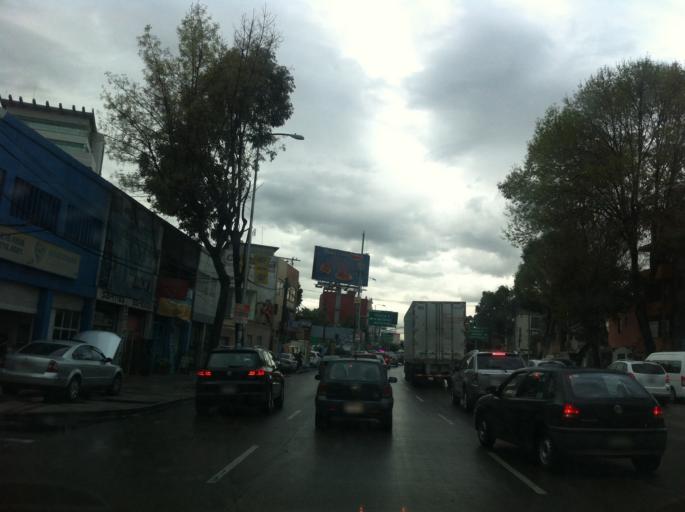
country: MX
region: Mexico City
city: Colonia del Valle
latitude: 19.3982
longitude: -99.1807
